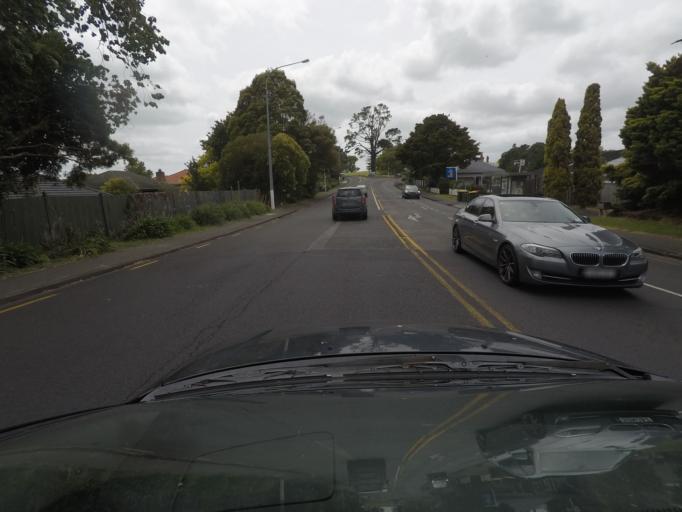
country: NZ
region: Auckland
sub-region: Auckland
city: Pakuranga
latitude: -36.8929
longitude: 174.9246
